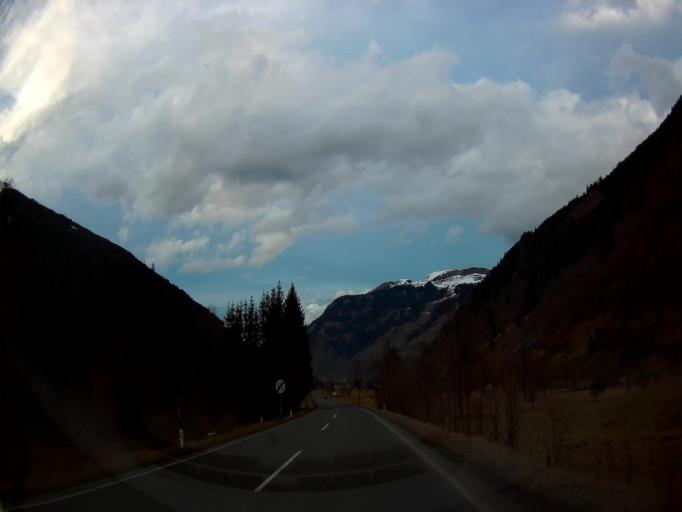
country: AT
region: Salzburg
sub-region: Politischer Bezirk Sankt Johann im Pongau
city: Dorfgastein
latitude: 47.2200
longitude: 13.1090
